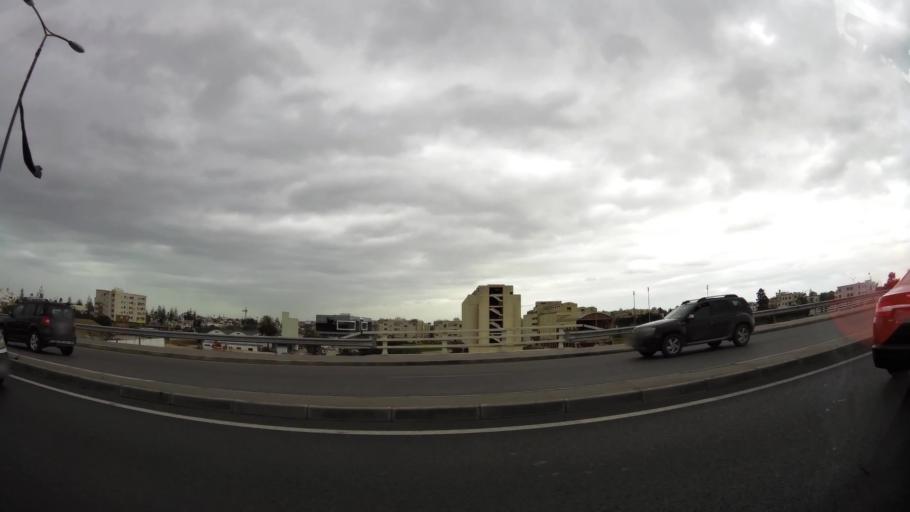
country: MA
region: Grand Casablanca
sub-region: Casablanca
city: Casablanca
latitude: 33.5478
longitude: -7.6434
